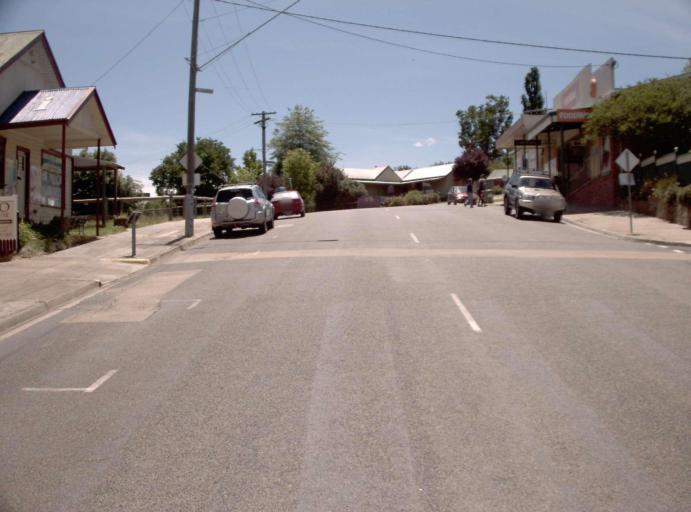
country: AU
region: Victoria
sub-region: Alpine
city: Mount Beauty
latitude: -37.0992
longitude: 147.5936
